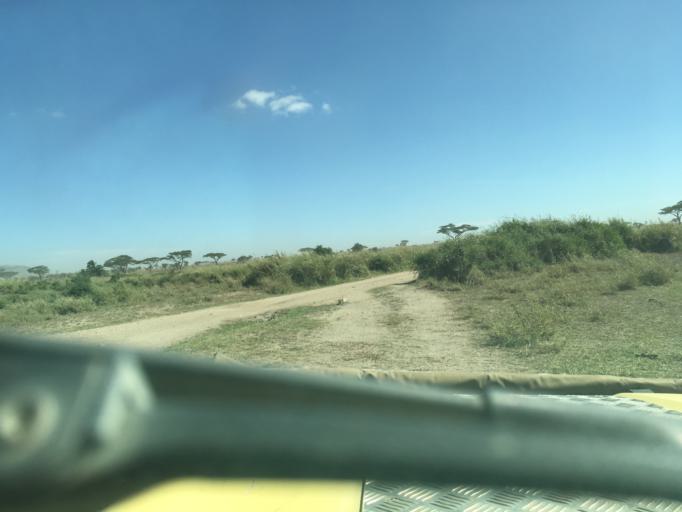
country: TZ
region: Mara
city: Mugumu
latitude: -2.4803
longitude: 34.8098
